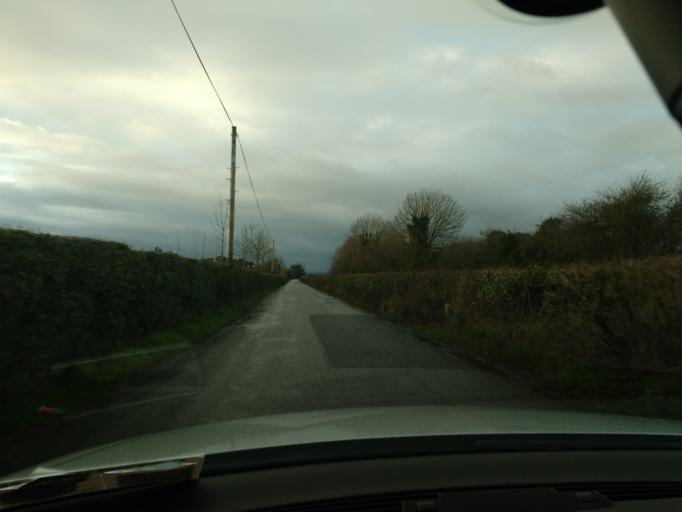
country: IE
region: Munster
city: Thurles
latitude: 52.6343
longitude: -7.8182
